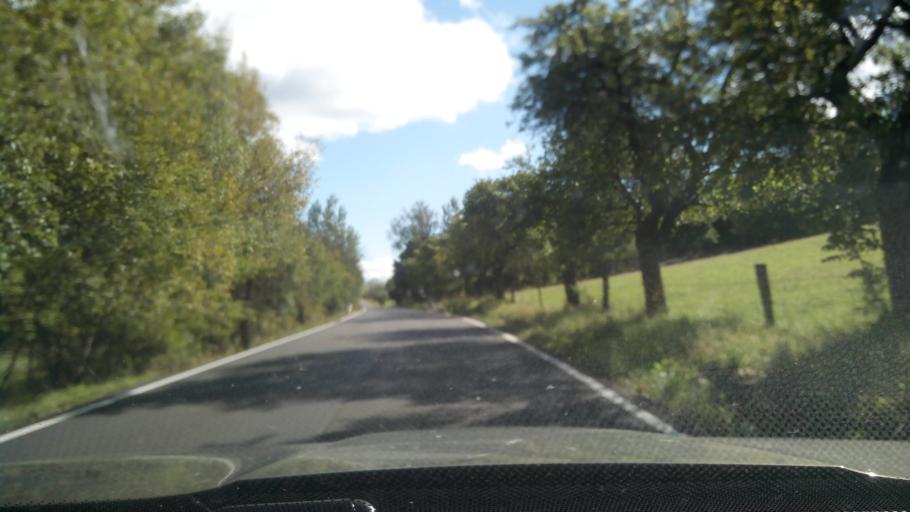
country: CZ
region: Jihocesky
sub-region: Okres Prachatice
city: Stachy
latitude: 49.1142
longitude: 13.6459
